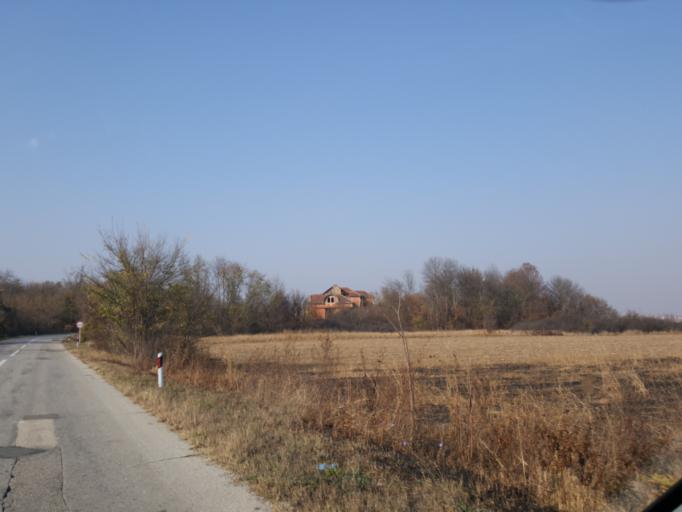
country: BG
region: Vidin
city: Bregovo
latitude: 44.1648
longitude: 22.5913
